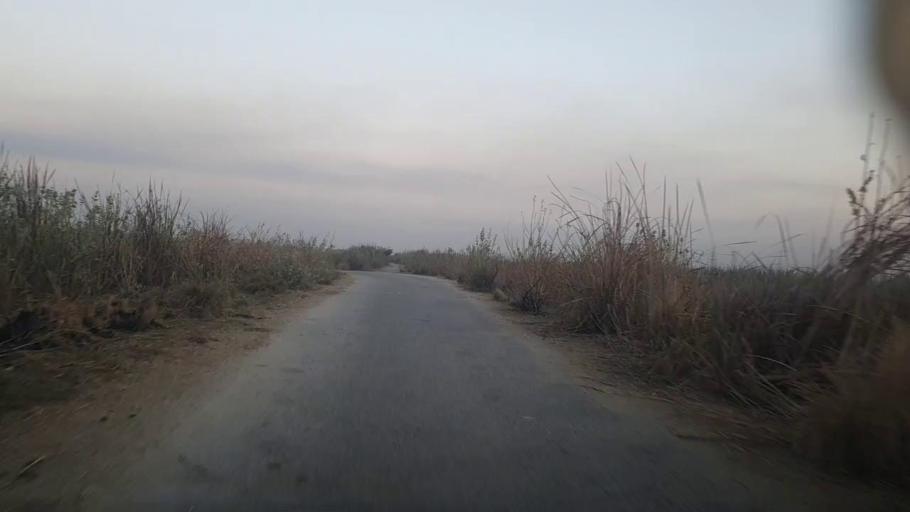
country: PK
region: Sindh
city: Kandiari
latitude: 26.6867
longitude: 68.9286
